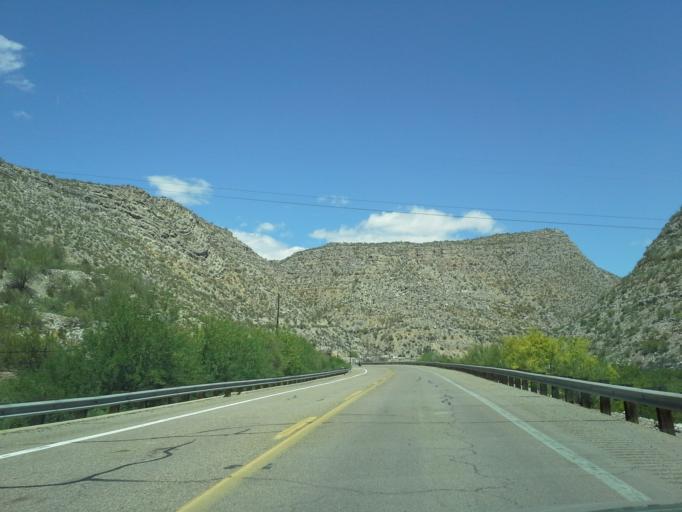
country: US
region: Arizona
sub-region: Pinal County
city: Kearny
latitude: 33.0009
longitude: -110.7666
